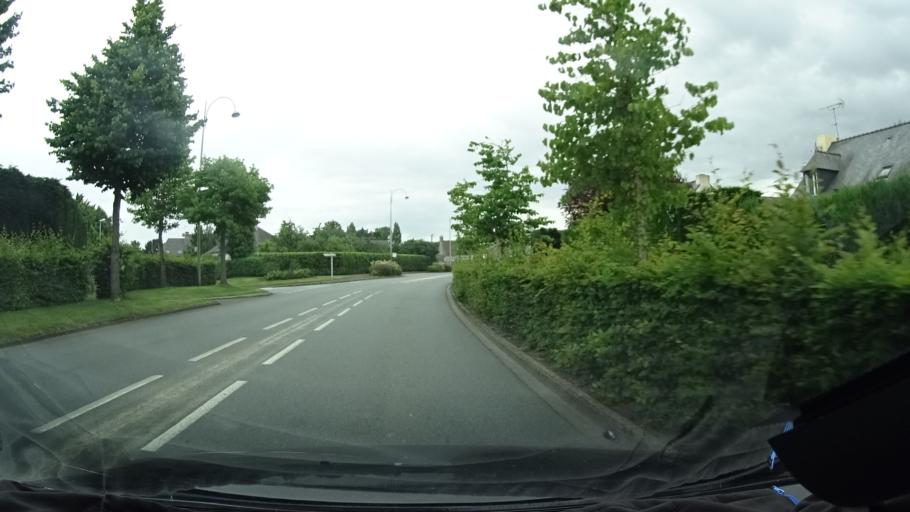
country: FR
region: Brittany
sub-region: Departement d'Ille-et-Vilaine
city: Saint-Malo
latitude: 48.6201
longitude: -2.0040
